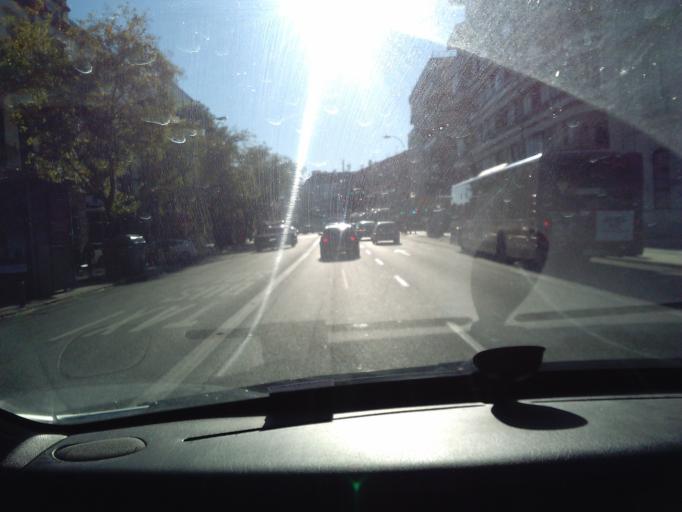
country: ES
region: Andalusia
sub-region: Provincia de Sevilla
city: Sevilla
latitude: 37.3950
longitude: -5.9831
